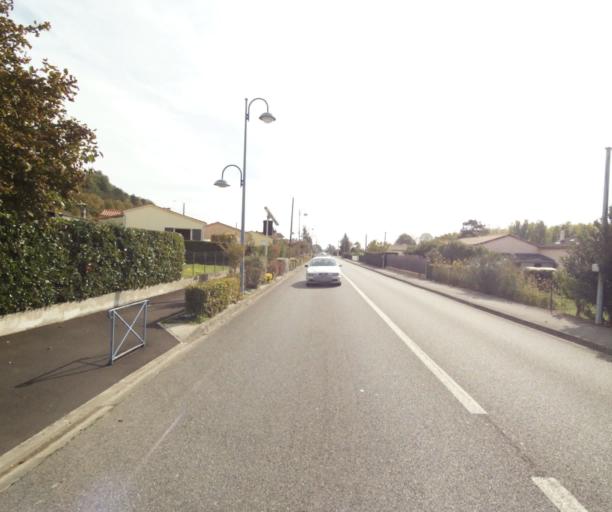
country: FR
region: Midi-Pyrenees
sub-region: Departement du Tarn-et-Garonne
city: Corbarieu
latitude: 43.9436
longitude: 1.3688
